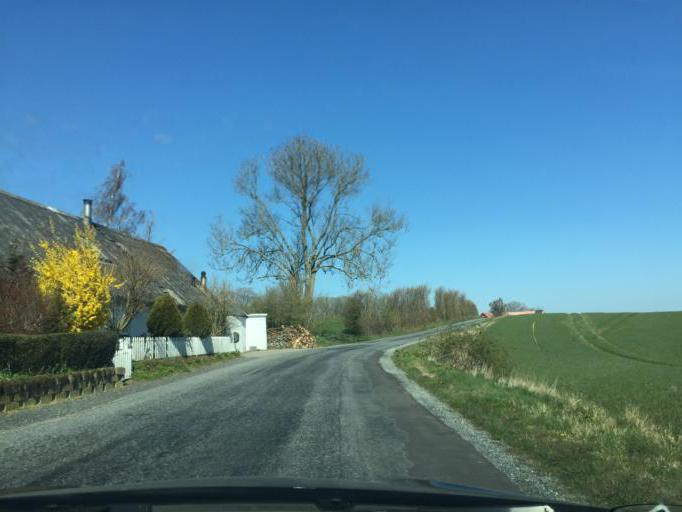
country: DK
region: South Denmark
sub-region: Faaborg-Midtfyn Kommune
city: Ringe
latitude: 55.2607
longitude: 10.5231
